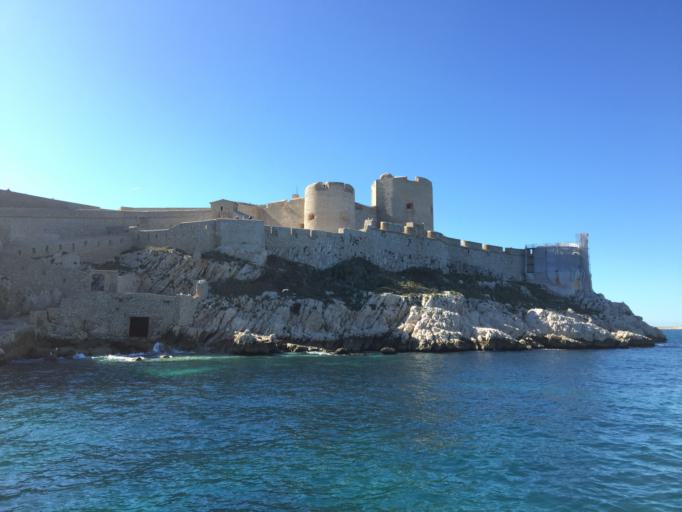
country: FR
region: Provence-Alpes-Cote d'Azur
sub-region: Departement des Bouches-du-Rhone
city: Marseille 07
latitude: 43.2809
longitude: 5.3266
